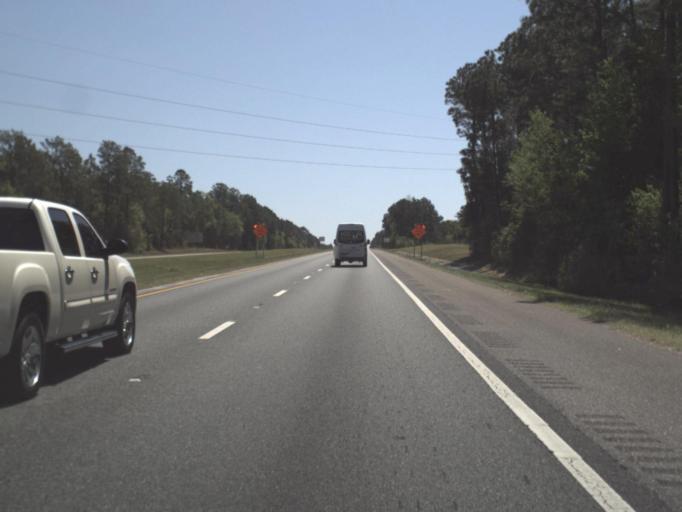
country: US
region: Florida
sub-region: Escambia County
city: Ensley
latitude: 30.5149
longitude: -87.3016
